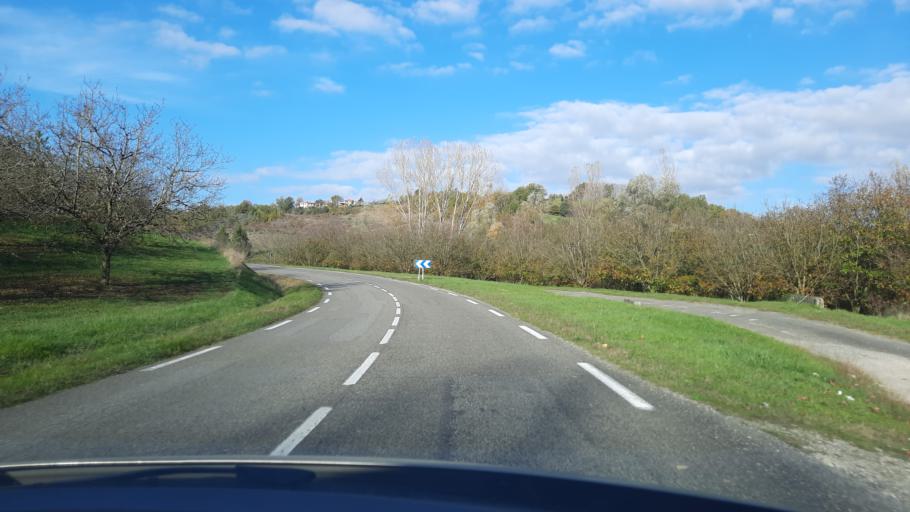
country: FR
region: Midi-Pyrenees
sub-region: Departement du Tarn-et-Garonne
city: Molieres
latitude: 44.1159
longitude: 1.3579
